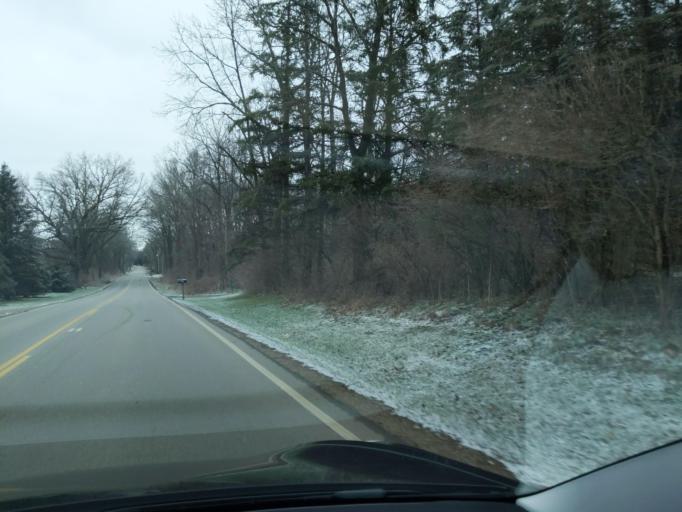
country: US
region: Michigan
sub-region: Jackson County
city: Spring Arbor
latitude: 42.2268
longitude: -84.5168
